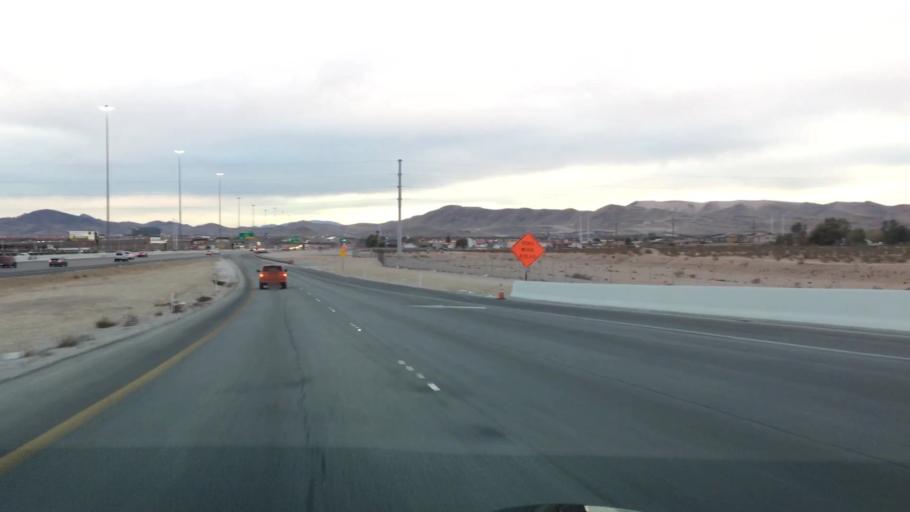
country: US
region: Nevada
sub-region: Clark County
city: Enterprise
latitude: 36.0117
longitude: -115.1810
